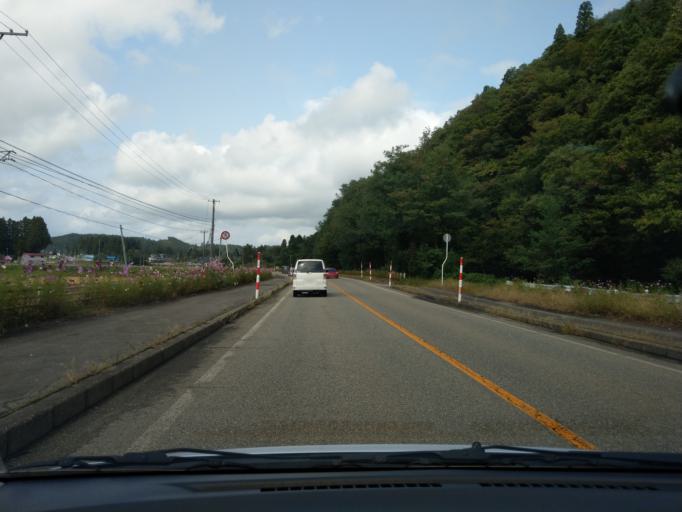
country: JP
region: Akita
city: Omagari
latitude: 39.4357
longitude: 140.3686
